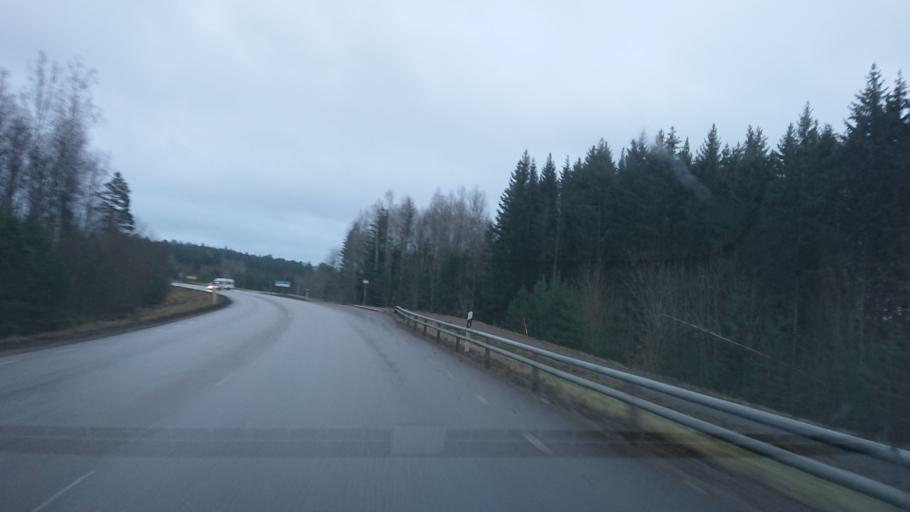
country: SE
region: Uppsala
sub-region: Osthammars Kommun
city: Bjorklinge
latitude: 60.0117
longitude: 17.5889
